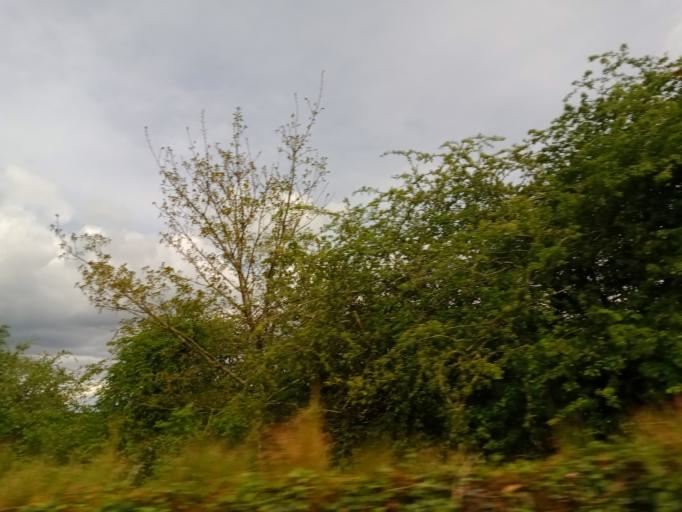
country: IE
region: Munster
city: Thurles
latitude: 52.6233
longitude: -7.7892
